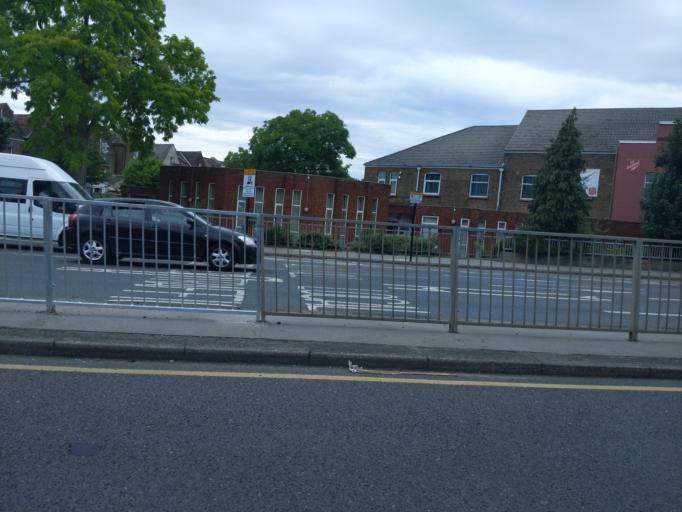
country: GB
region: England
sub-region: Greater London
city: Croydon
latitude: 51.3735
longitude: -0.1066
